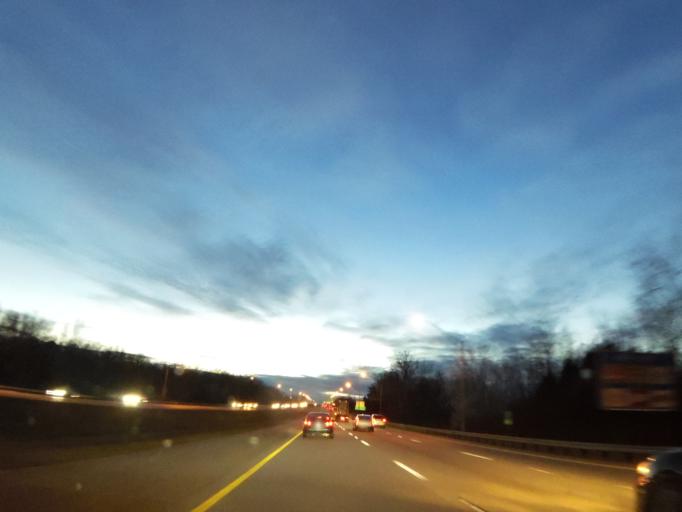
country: US
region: Kentucky
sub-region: Jefferson County
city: Middletown
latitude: 38.2233
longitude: -85.5211
